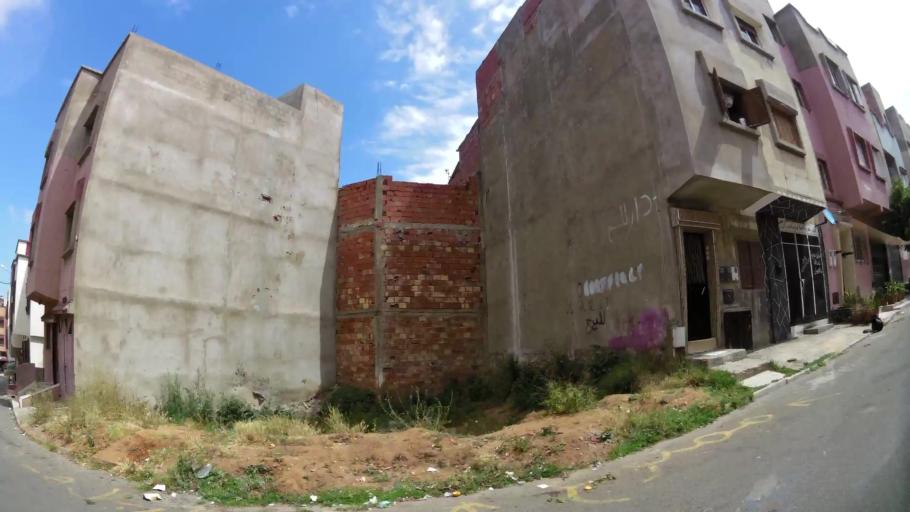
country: MA
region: Gharb-Chrarda-Beni Hssen
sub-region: Kenitra Province
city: Kenitra
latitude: 34.2454
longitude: -6.6113
